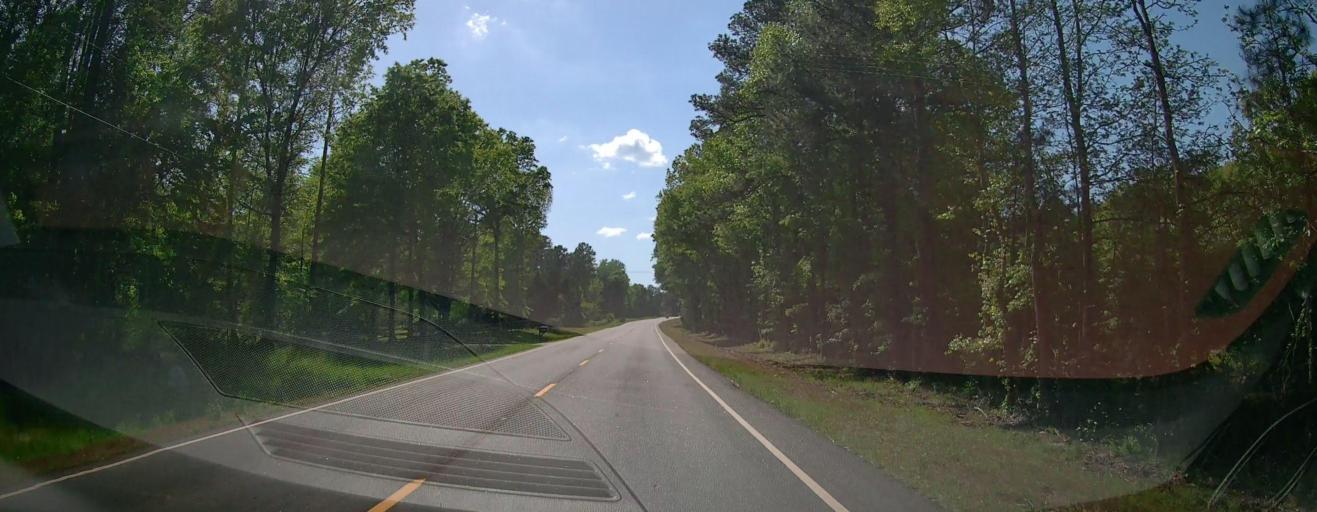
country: US
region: Georgia
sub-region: Morgan County
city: Madison
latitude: 33.6074
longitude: -83.3555
